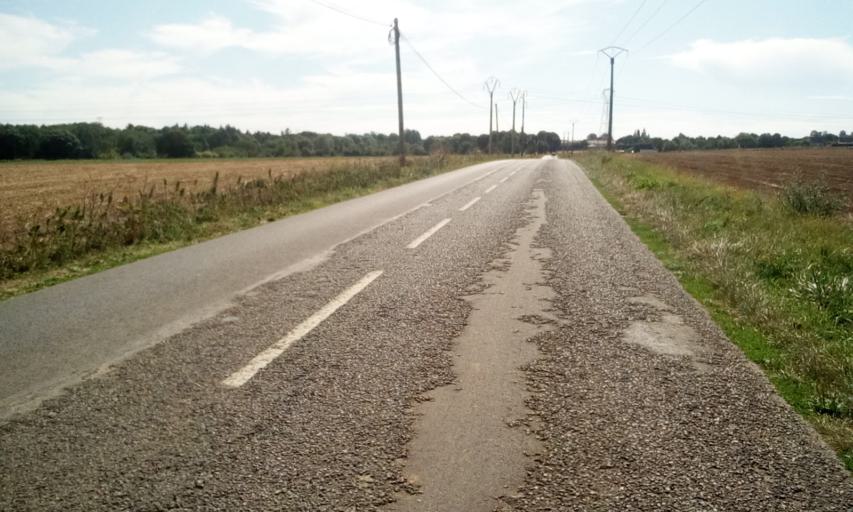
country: FR
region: Lower Normandy
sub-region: Departement du Calvados
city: Eterville
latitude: 49.1379
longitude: -0.4088
